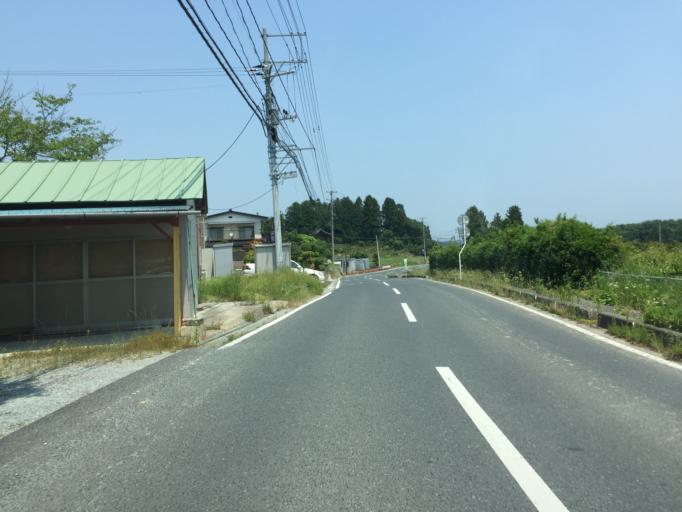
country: JP
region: Miyagi
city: Marumori
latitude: 37.8242
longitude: 140.8949
